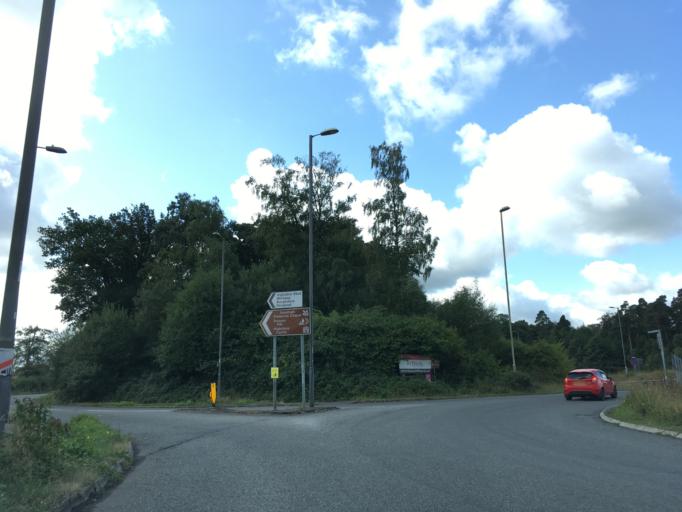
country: GB
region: England
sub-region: Hampshire
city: Highclere
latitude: 51.3478
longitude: -1.3380
